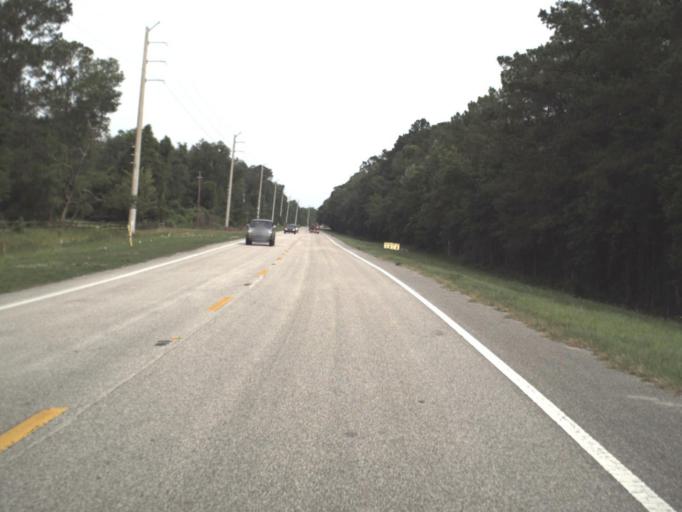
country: US
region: Florida
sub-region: Saint Johns County
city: Saint Augustine
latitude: 29.9453
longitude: -81.4434
